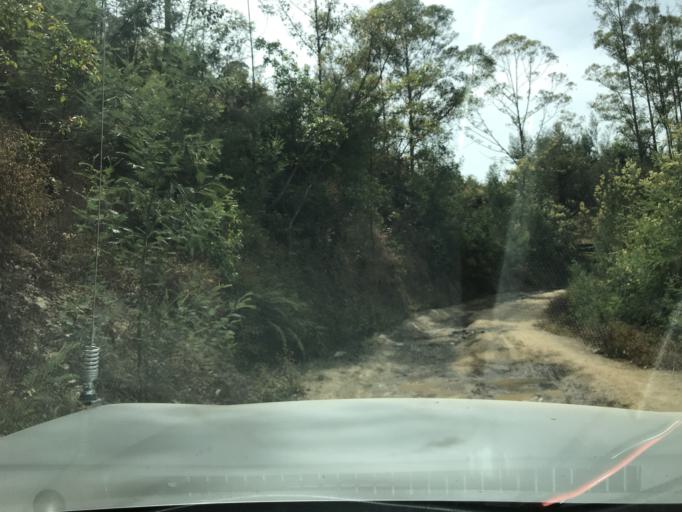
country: TL
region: Ainaro
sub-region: Ainaro
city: Ainaro
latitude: -8.8834
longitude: 125.5237
